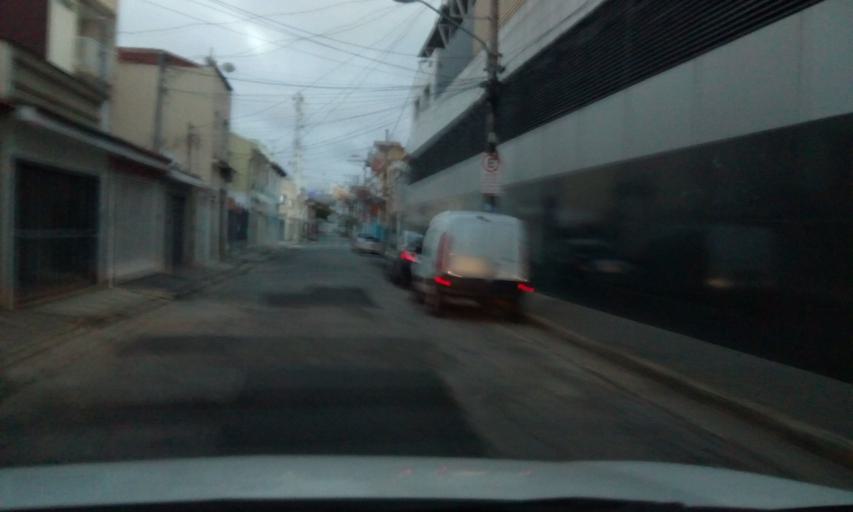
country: BR
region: Sao Paulo
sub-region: Sao Paulo
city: Sao Paulo
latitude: -23.5390
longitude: -46.5842
